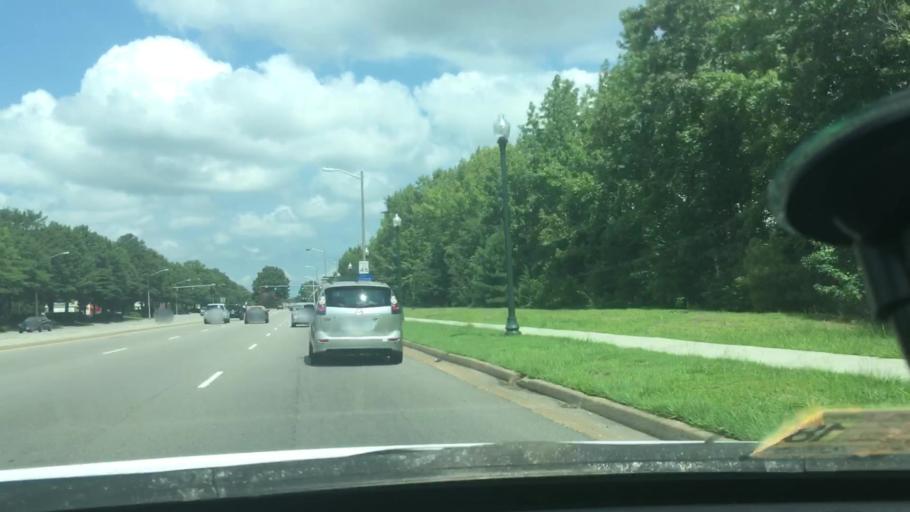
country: US
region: Virginia
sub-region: City of Chesapeake
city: Chesapeake
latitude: 36.7695
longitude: -76.2276
